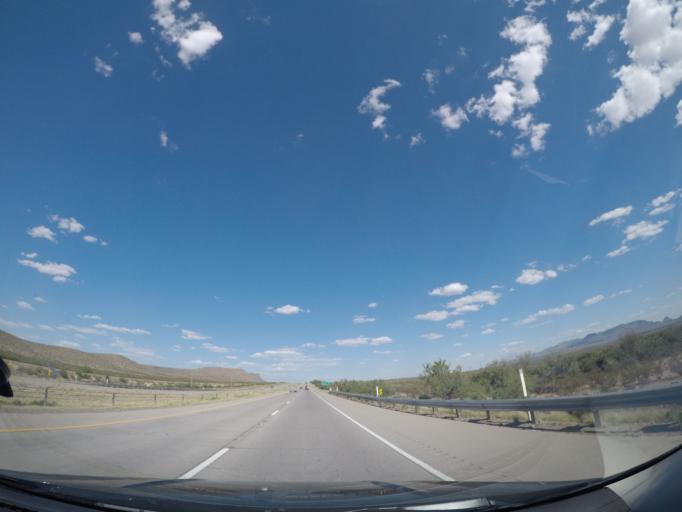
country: US
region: Texas
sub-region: Hudspeth County
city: Sierra Blanca
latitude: 31.1252
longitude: -105.1888
